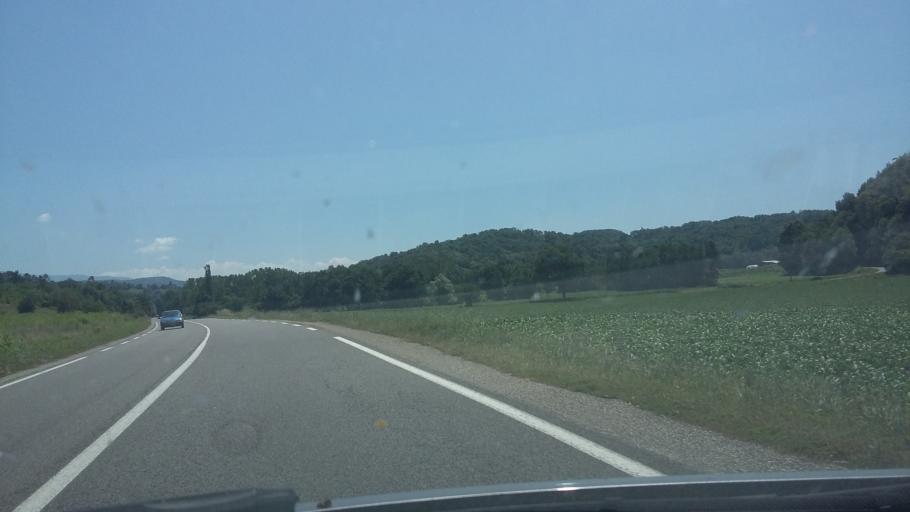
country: FR
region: Rhone-Alpes
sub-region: Departement de l'Ain
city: Belley
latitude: 45.7891
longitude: 5.6836
